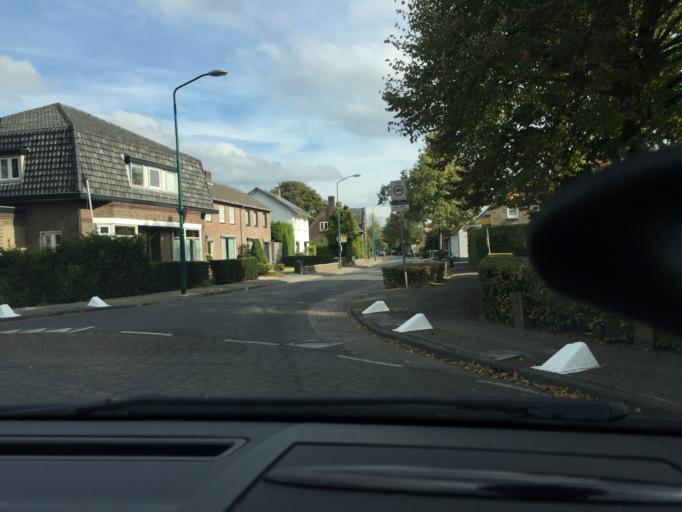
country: NL
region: North Brabant
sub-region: Gemeente Laarbeek
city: Aarle-Rixtel
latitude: 51.5088
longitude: 5.6308
